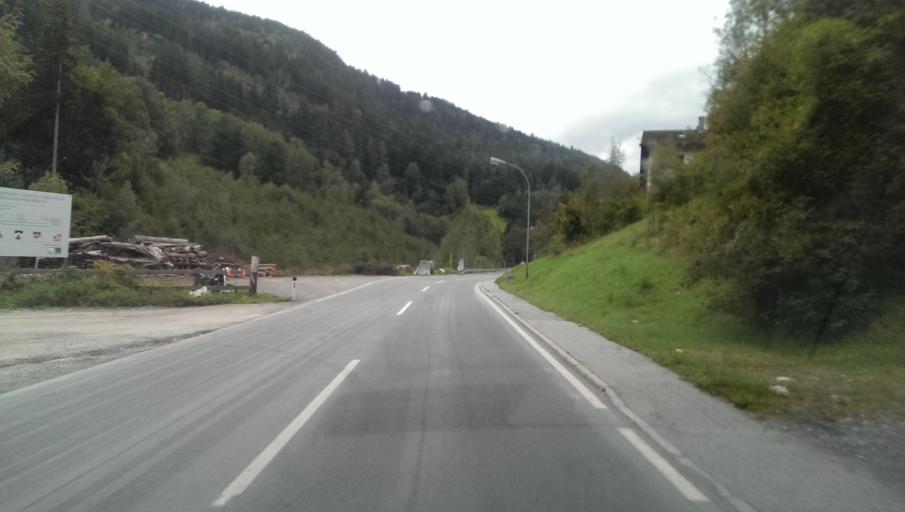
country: AT
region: Tyrol
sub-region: Politischer Bezirk Landeck
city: Grins
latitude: 47.1382
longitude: 10.5312
